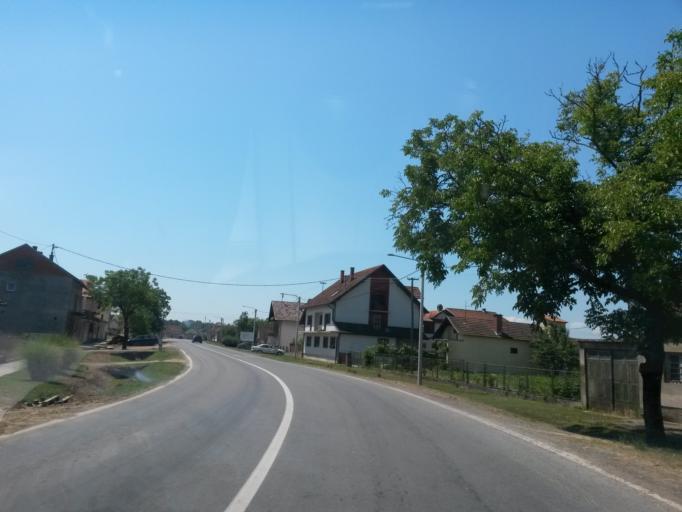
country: HR
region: Brodsko-Posavska
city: Krusevica
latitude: 45.0736
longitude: 18.4813
